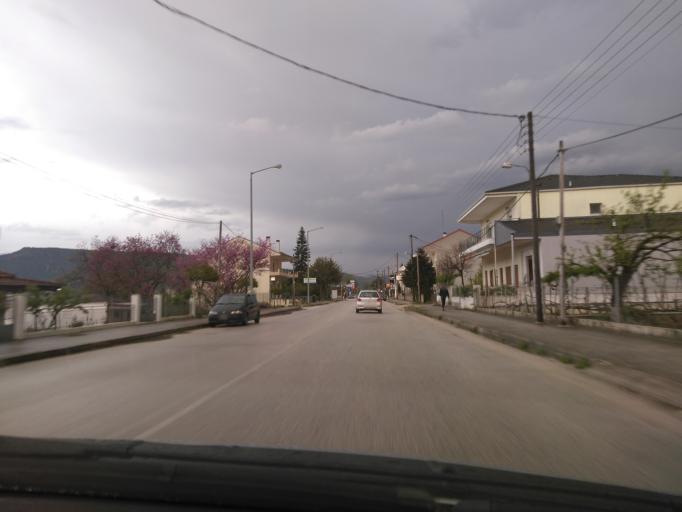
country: GR
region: Epirus
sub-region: Nomos Ioanninon
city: Katsikas
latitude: 39.6277
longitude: 20.8819
